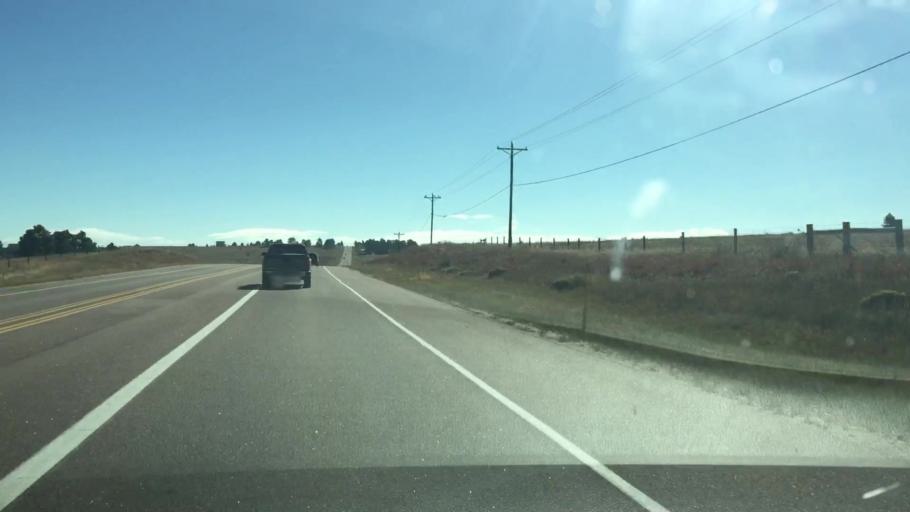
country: US
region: Colorado
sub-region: Elbert County
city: Elizabeth
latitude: 39.3603
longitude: -104.5412
